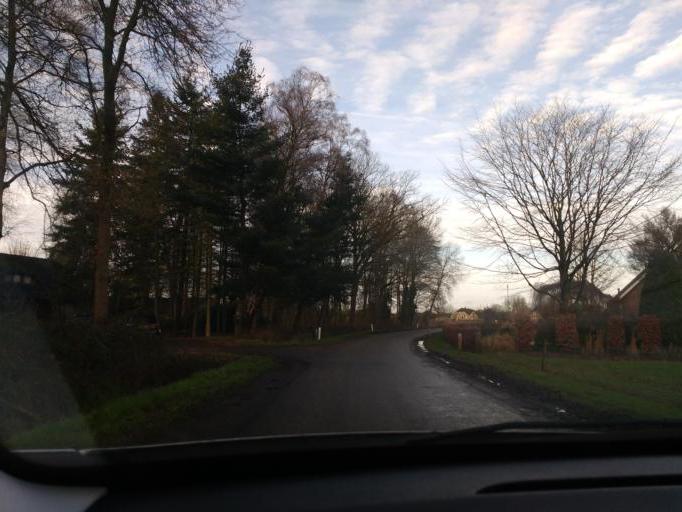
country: NL
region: Limburg
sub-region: Gemeente Venray
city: Venray
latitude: 51.5107
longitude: 5.9324
